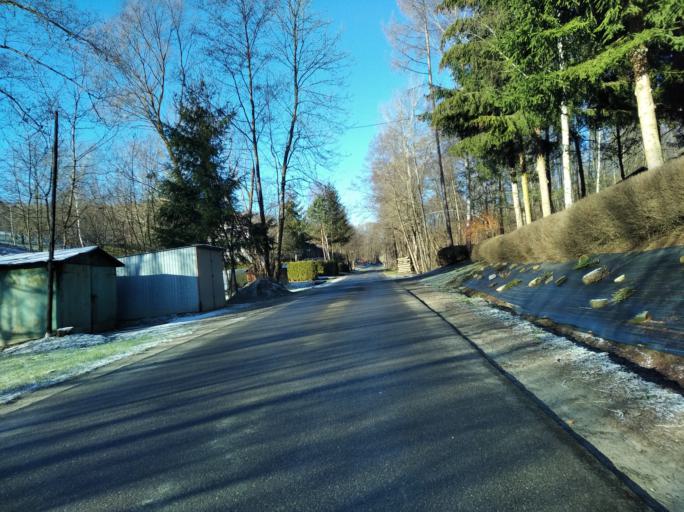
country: PL
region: Subcarpathian Voivodeship
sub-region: Powiat strzyzowski
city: Czudec
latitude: 49.9518
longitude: 21.7748
